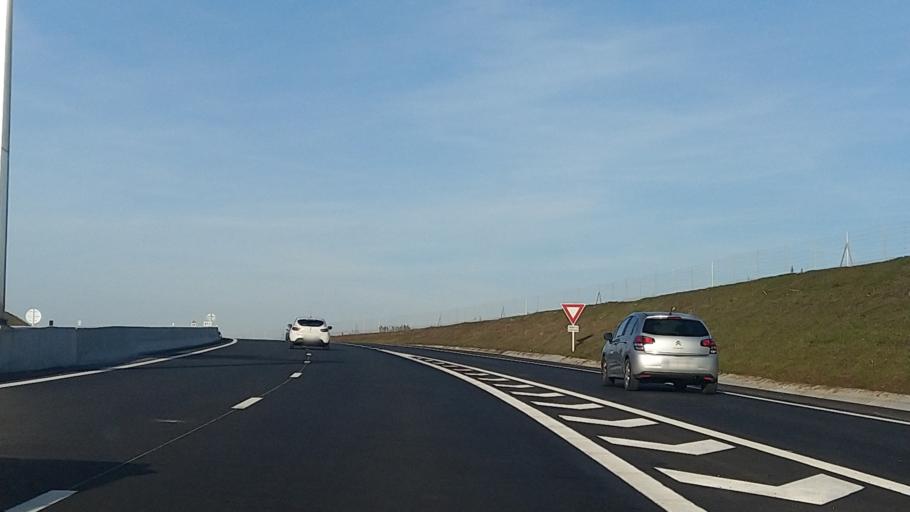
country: FR
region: Ile-de-France
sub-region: Departement du Val-d'Oise
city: Montsoult
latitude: 49.0721
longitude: 2.3325
